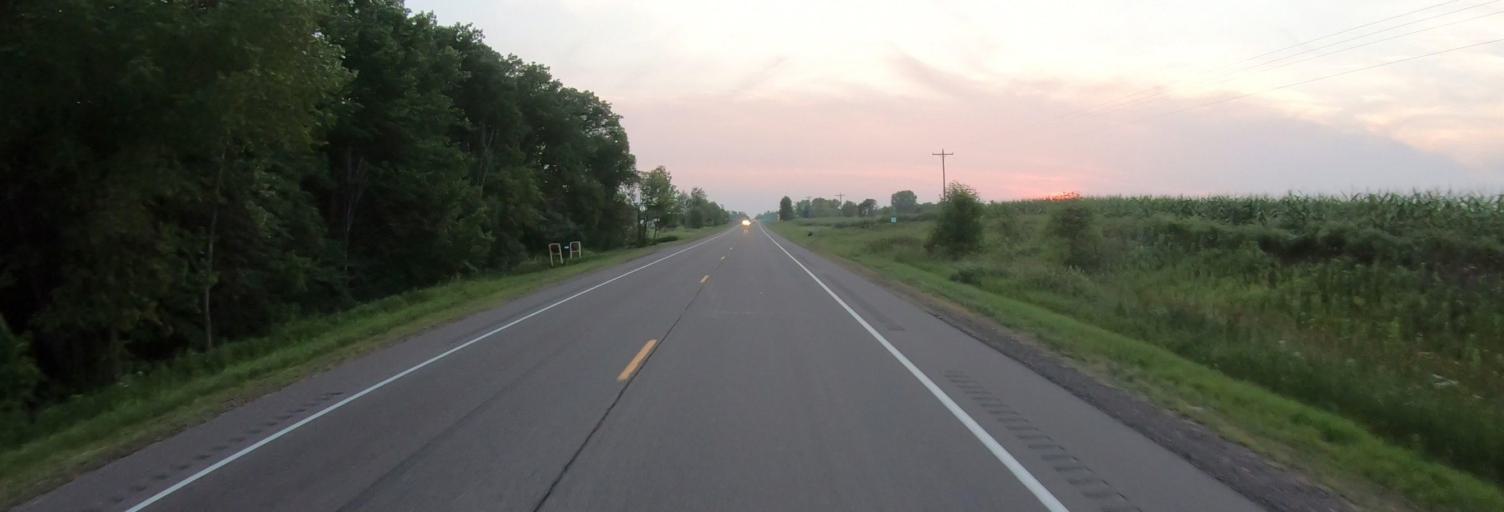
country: US
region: Minnesota
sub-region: Pine County
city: Rock Creek
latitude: 45.7666
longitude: -92.9775
